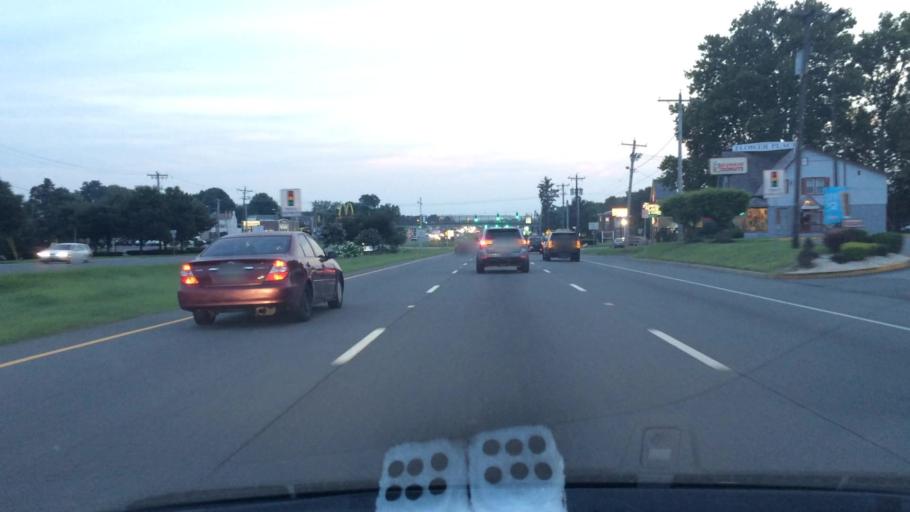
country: US
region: Delaware
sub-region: New Castle County
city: Wilmington Manor
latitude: 39.6879
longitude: -75.5839
